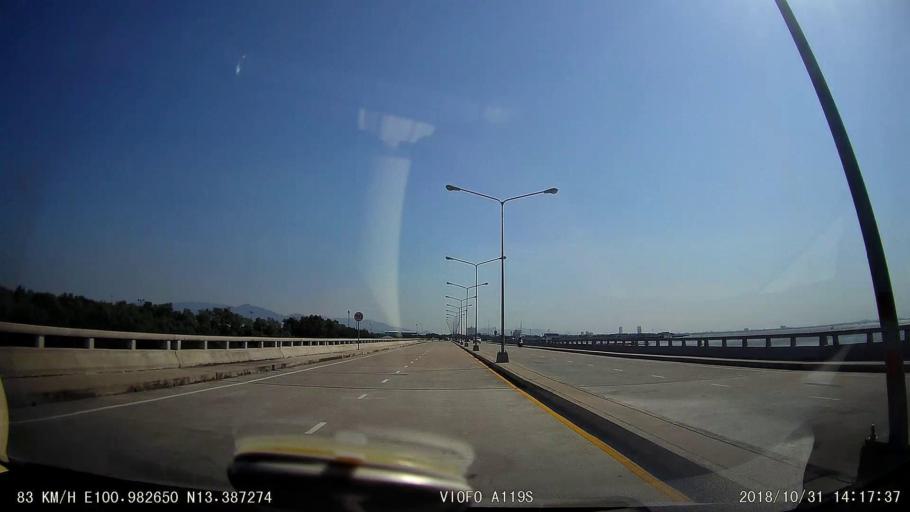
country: TH
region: Chon Buri
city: Chon Buri
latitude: 13.3869
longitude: 100.9827
